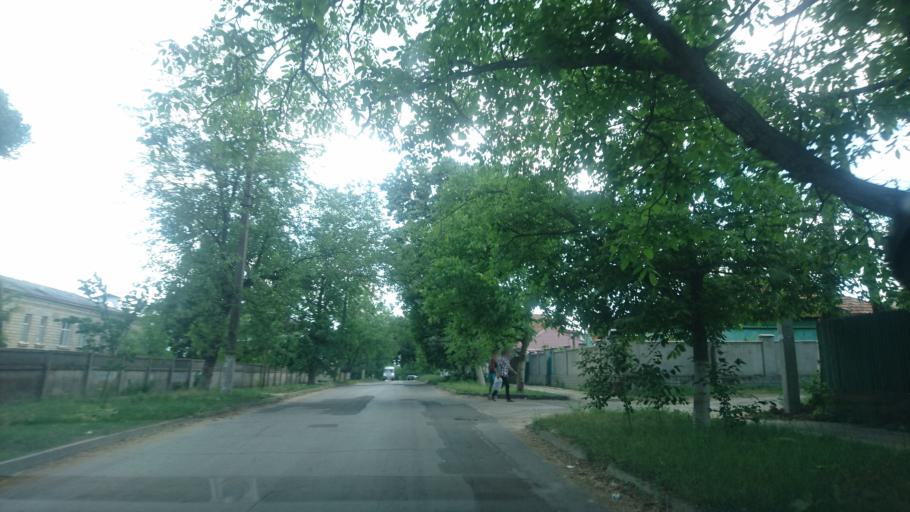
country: MD
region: Chisinau
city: Chisinau
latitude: 47.0519
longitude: 28.8444
